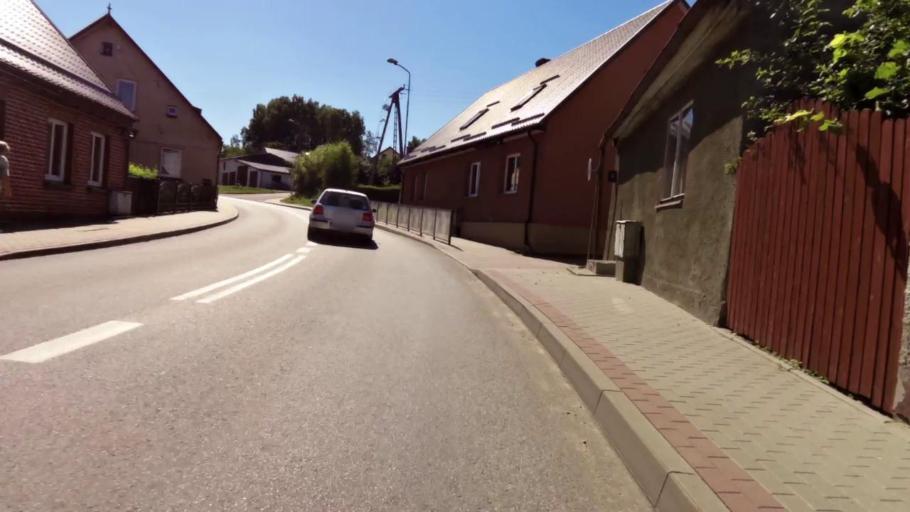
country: PL
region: West Pomeranian Voivodeship
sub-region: Powiat szczecinecki
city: Bialy Bor
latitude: 53.8955
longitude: 16.8321
